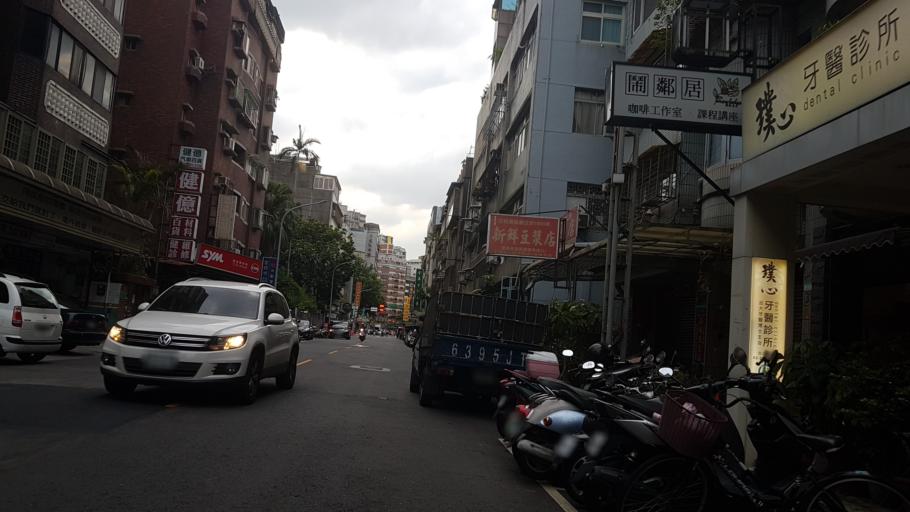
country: TW
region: Taipei
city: Taipei
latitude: 25.0294
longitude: 121.5234
